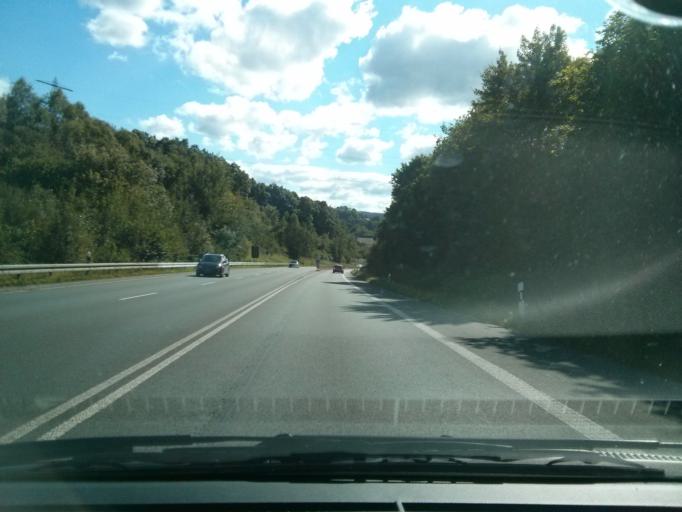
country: DE
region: North Rhine-Westphalia
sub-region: Regierungsbezirk Arnsberg
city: Arnsberg
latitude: 51.4164
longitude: 8.0547
